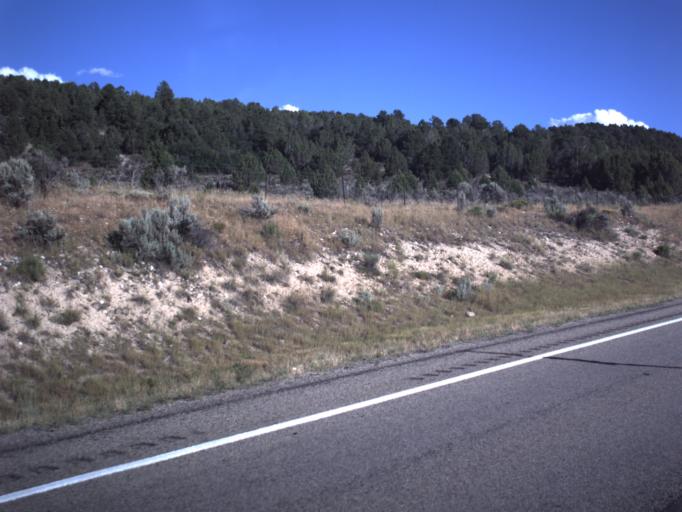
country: US
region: Utah
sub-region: Sanpete County
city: Fairview
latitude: 39.7458
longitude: -111.4775
